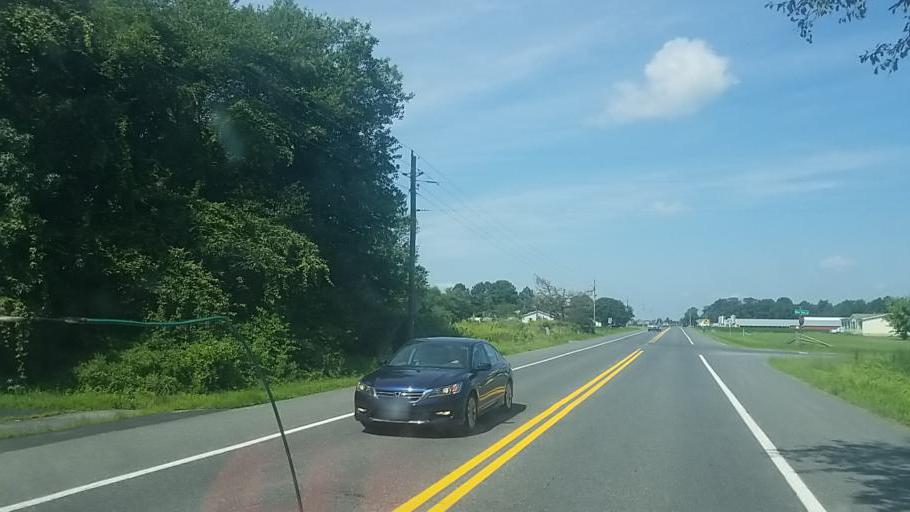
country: US
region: Delaware
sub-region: Sussex County
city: Bridgeville
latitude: 38.8245
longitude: -75.6449
